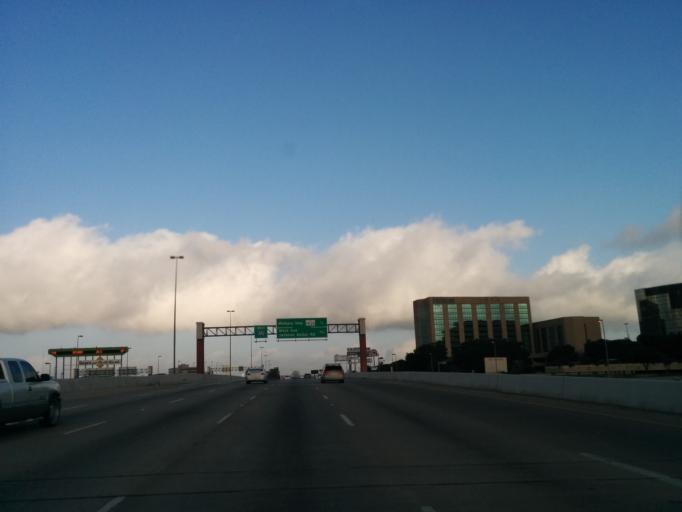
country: US
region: Texas
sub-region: Bexar County
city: Castle Hills
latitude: 29.5207
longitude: -98.4992
